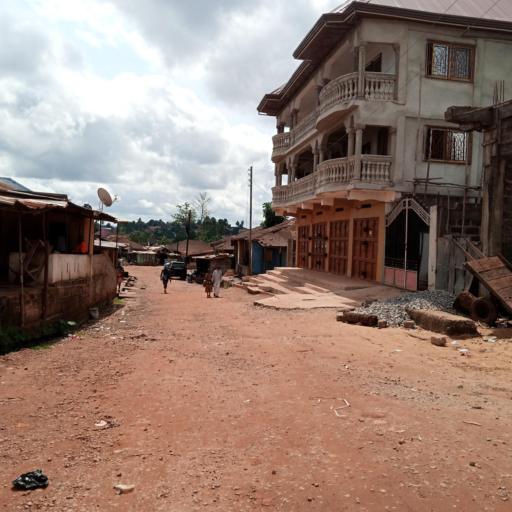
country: SL
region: Southern Province
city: Bo
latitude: 7.9638
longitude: -11.7380
